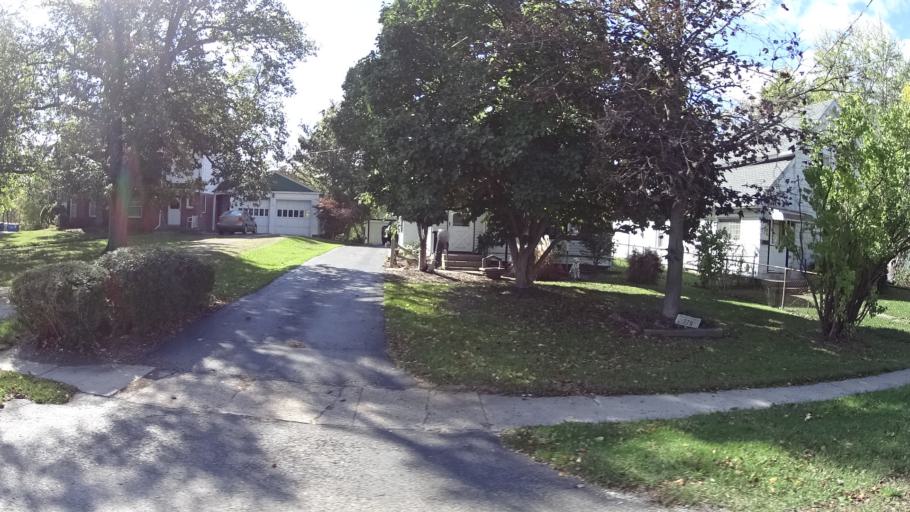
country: US
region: Ohio
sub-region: Lorain County
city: Grafton
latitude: 41.2749
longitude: -82.0600
